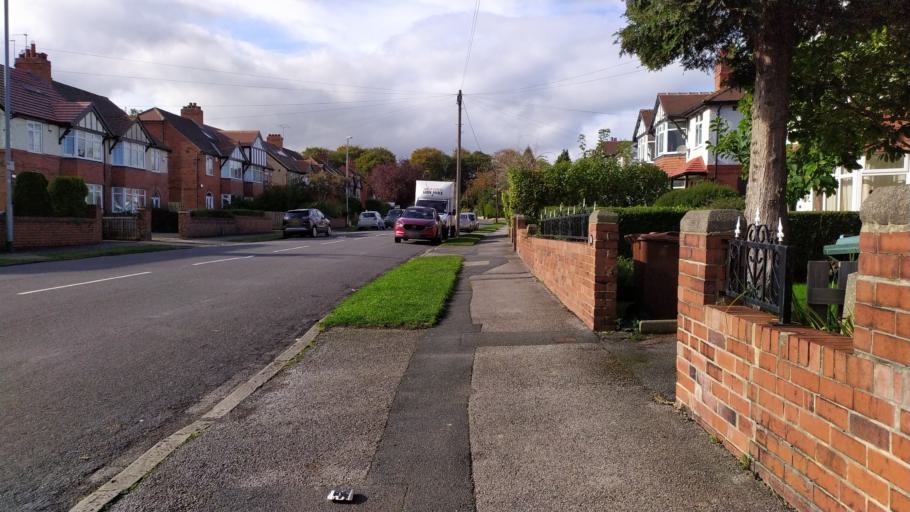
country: GB
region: England
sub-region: City and Borough of Leeds
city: Leeds
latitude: 53.8223
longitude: -1.5846
